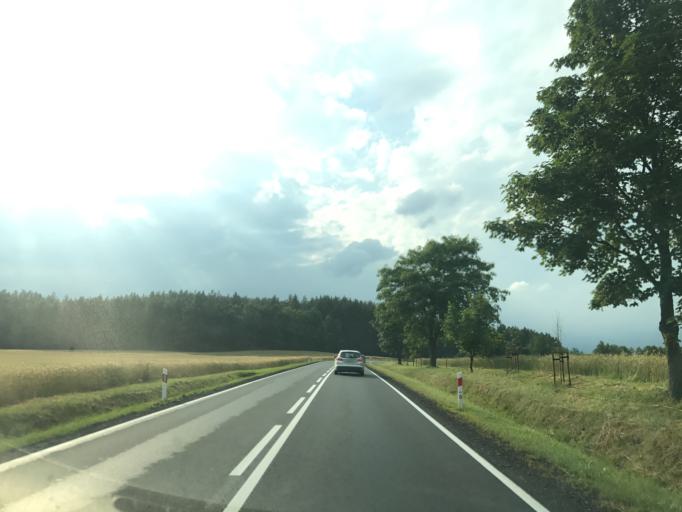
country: PL
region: Pomeranian Voivodeship
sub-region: Powiat czluchowski
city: Przechlewo
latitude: 53.7126
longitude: 17.2523
